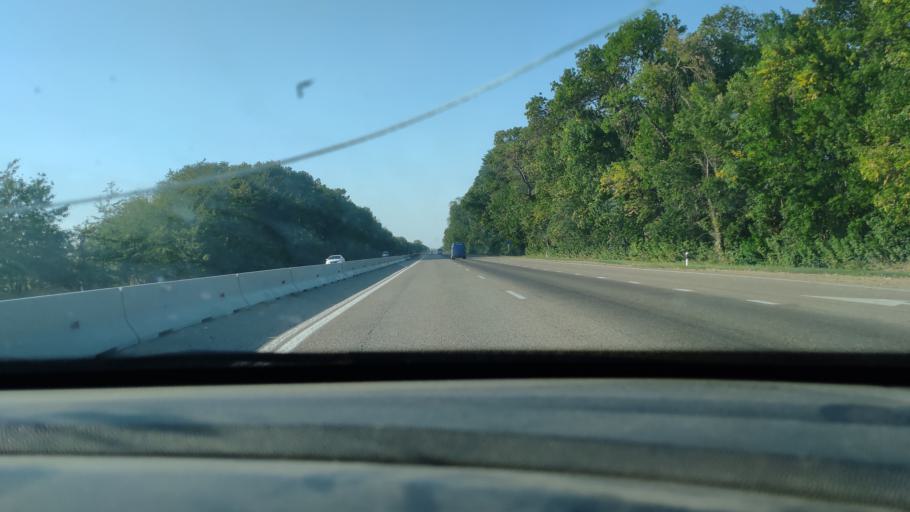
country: RU
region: Krasnodarskiy
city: Timashevsk
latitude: 45.5380
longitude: 38.9368
